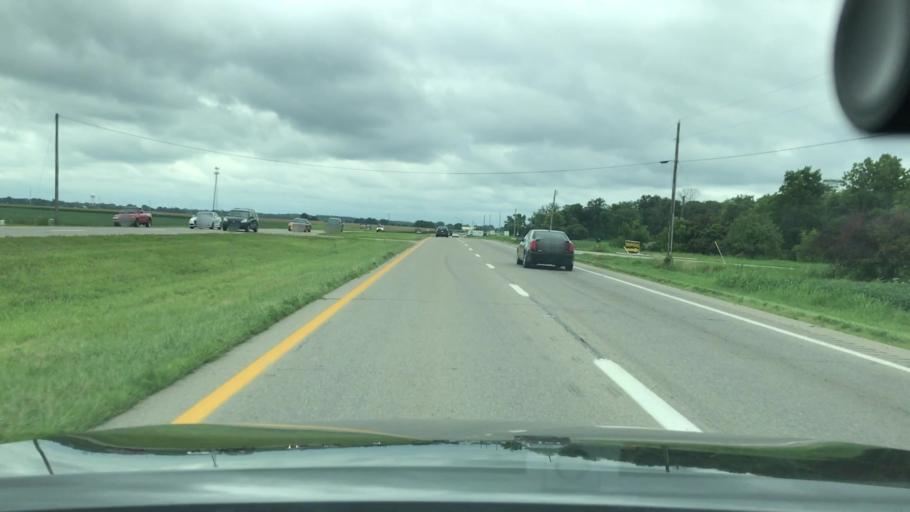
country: US
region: Ohio
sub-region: Pickaway County
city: South Bloomfield
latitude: 39.7421
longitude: -82.9879
